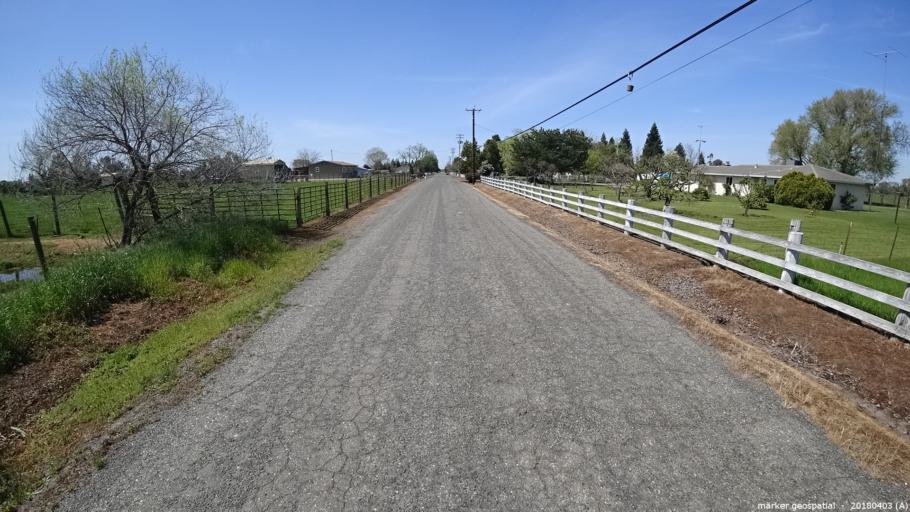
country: US
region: California
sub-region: Sacramento County
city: Wilton
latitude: 38.3873
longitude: -121.2643
